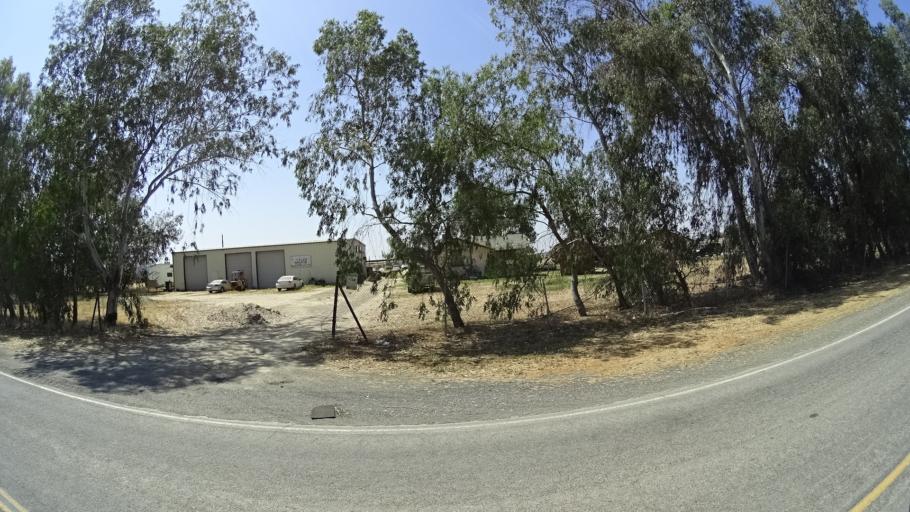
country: US
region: California
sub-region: Kings County
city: Home Garden
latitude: 36.3135
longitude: -119.6094
